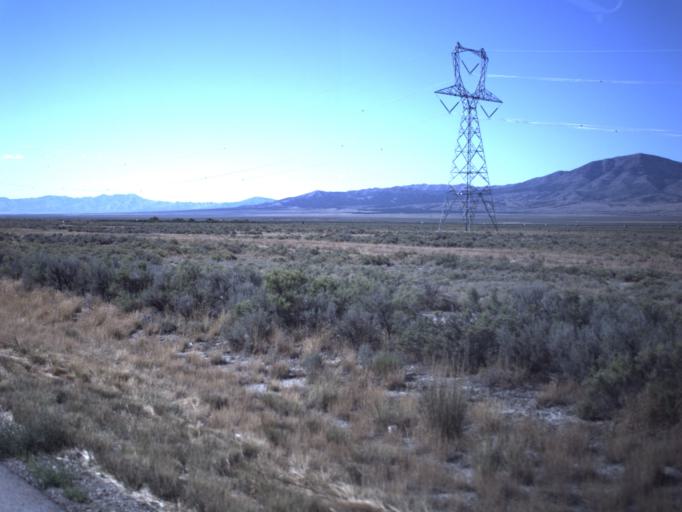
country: US
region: Utah
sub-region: Tooele County
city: Tooele
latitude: 40.3421
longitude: -112.4106
